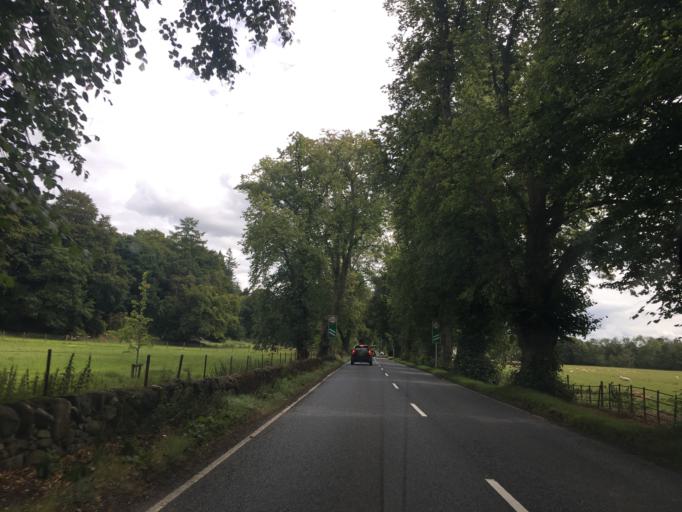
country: GB
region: Scotland
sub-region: Stirling
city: Callander
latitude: 56.2458
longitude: -4.2351
